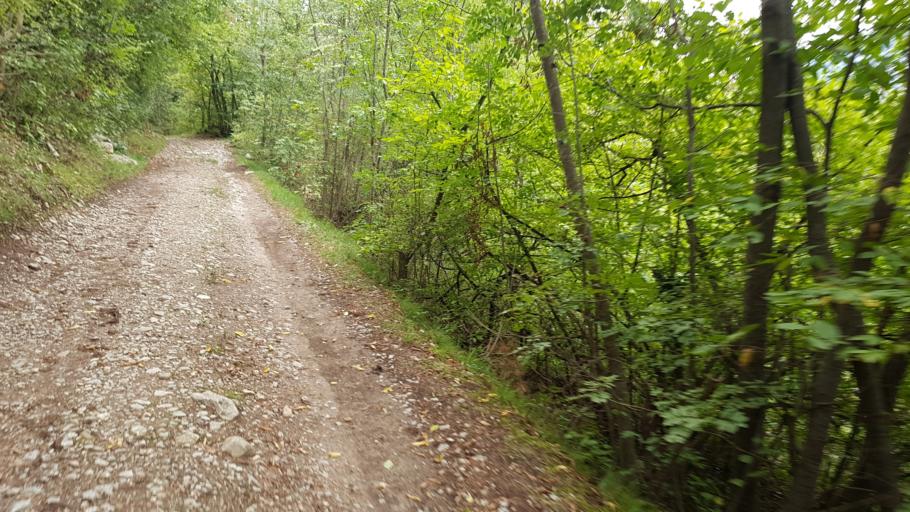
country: IT
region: Trentino-Alto Adige
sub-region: Provincia di Trento
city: Cavedine
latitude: 46.0066
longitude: 10.9720
